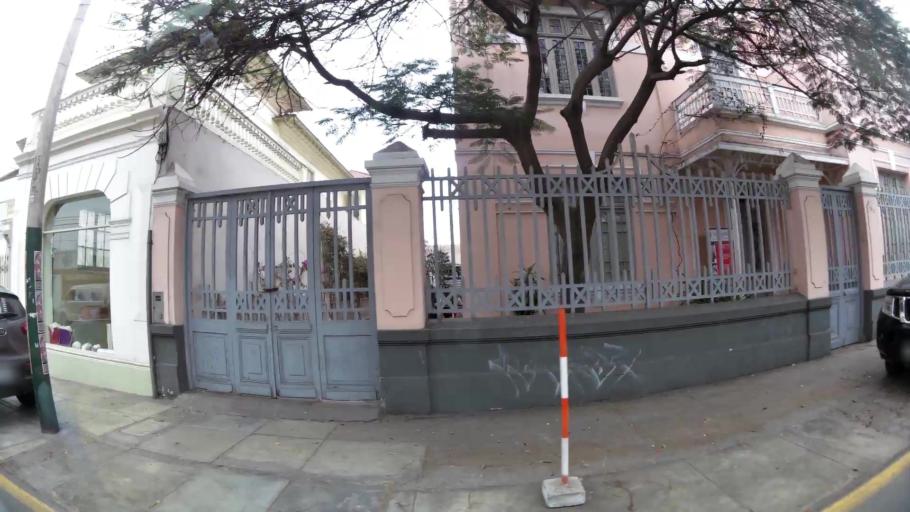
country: PE
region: Lima
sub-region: Lima
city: Surco
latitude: -12.1452
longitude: -77.0230
